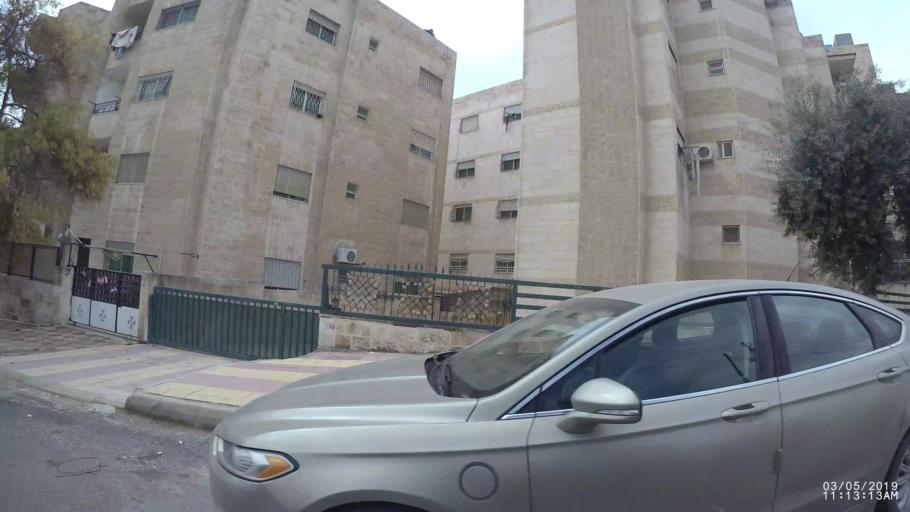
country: JO
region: Amman
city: Amman
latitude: 31.9915
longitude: 35.9269
